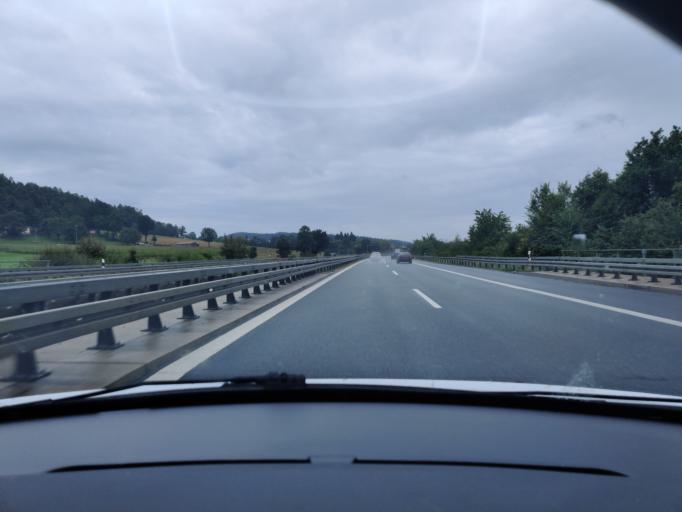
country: DE
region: Bavaria
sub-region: Upper Palatinate
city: Pfreimd
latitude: 49.5049
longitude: 12.1814
